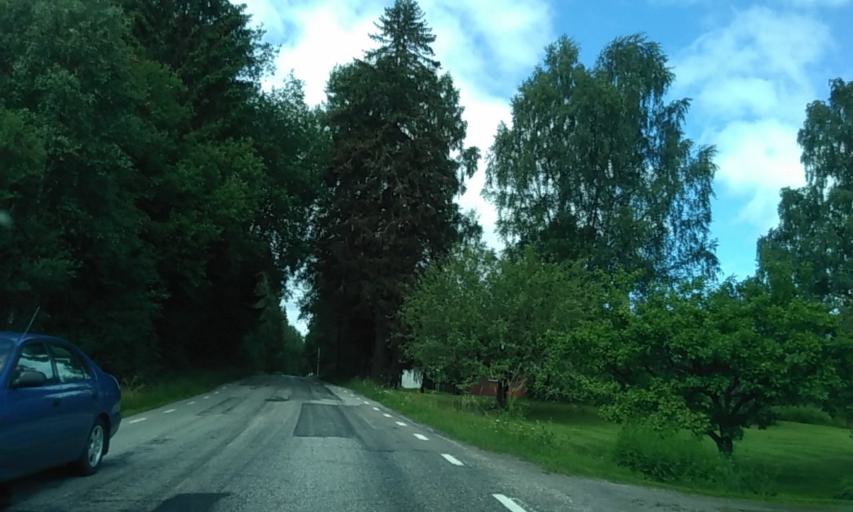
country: SE
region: Vaestra Goetaland
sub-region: Vargarda Kommun
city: Vargarda
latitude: 58.1087
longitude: 12.8063
